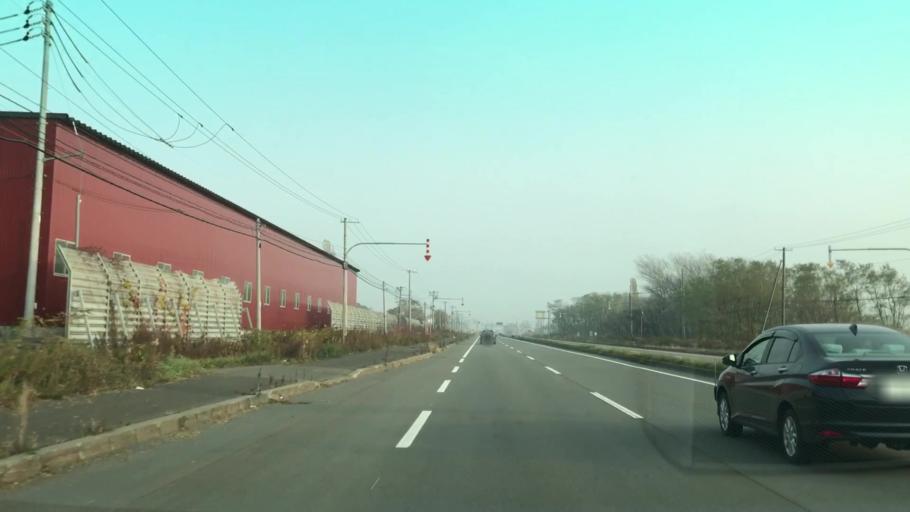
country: JP
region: Hokkaido
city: Ishikari
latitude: 43.2090
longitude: 141.3334
